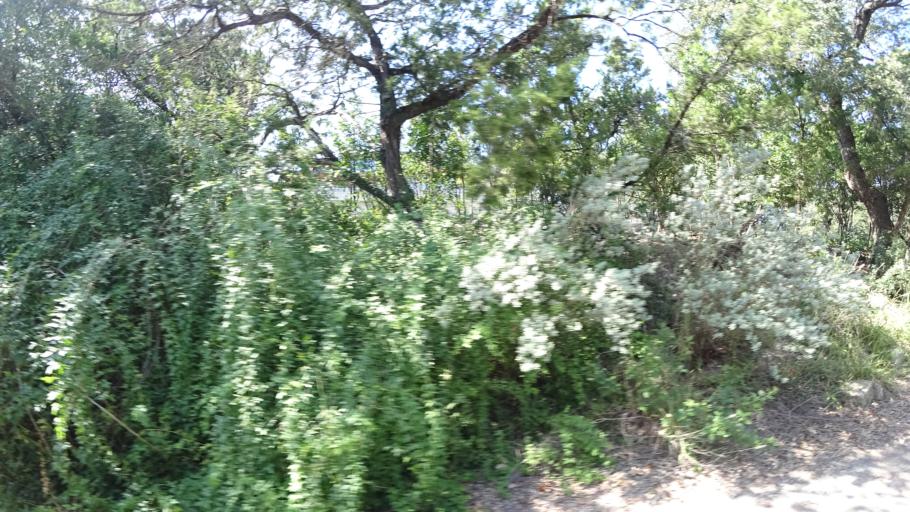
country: US
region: Texas
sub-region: Travis County
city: West Lake Hills
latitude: 30.3047
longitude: -97.8026
